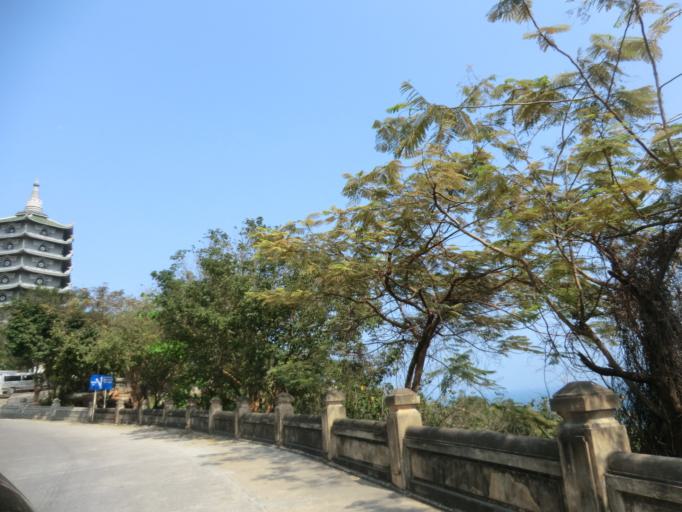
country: VN
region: Da Nang
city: Son Tra
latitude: 16.0995
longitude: 108.2788
